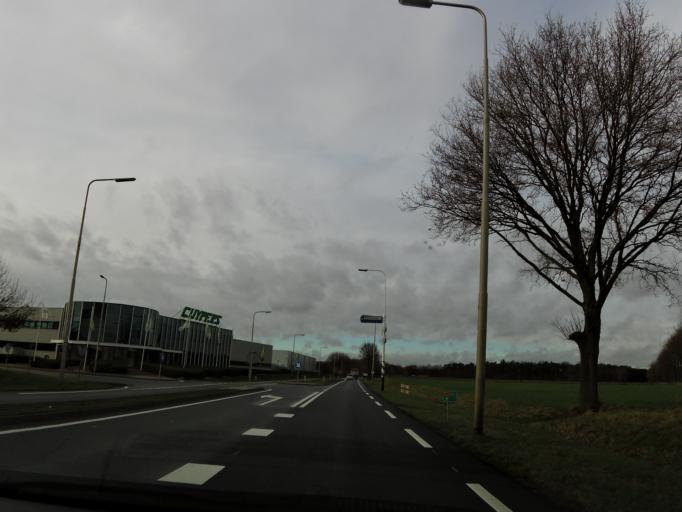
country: NL
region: Limburg
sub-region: Gemeente Roerdalen
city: Posterholt
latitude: 51.1290
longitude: 6.0296
